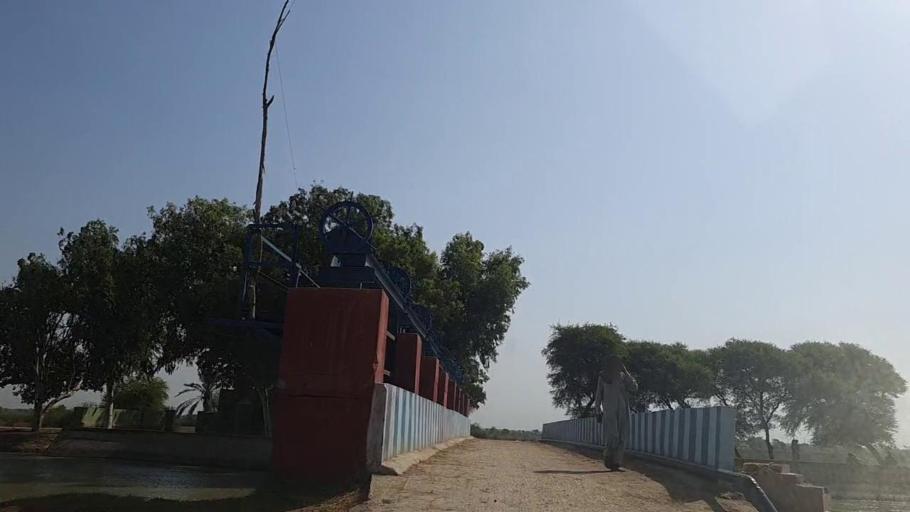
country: PK
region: Sindh
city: Daro Mehar
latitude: 24.7218
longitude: 68.0747
